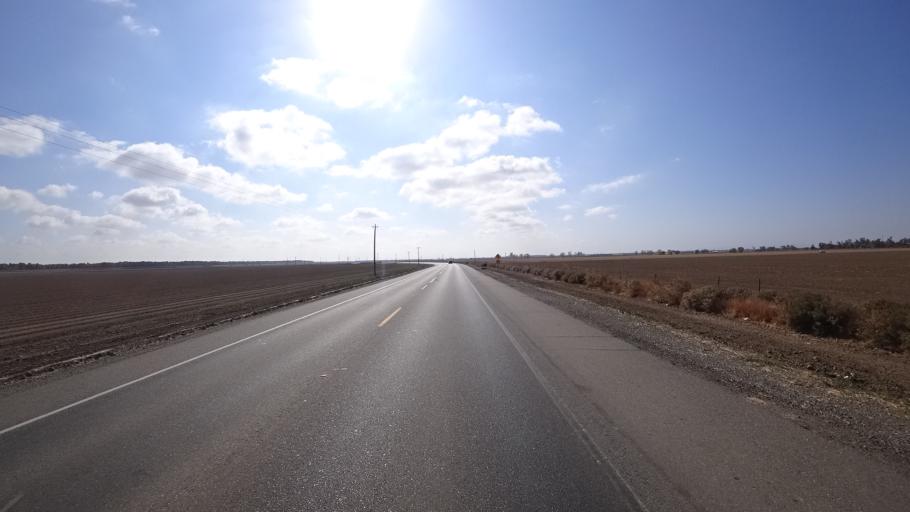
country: US
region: California
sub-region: Yolo County
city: Woodland
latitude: 38.7187
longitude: -121.7303
